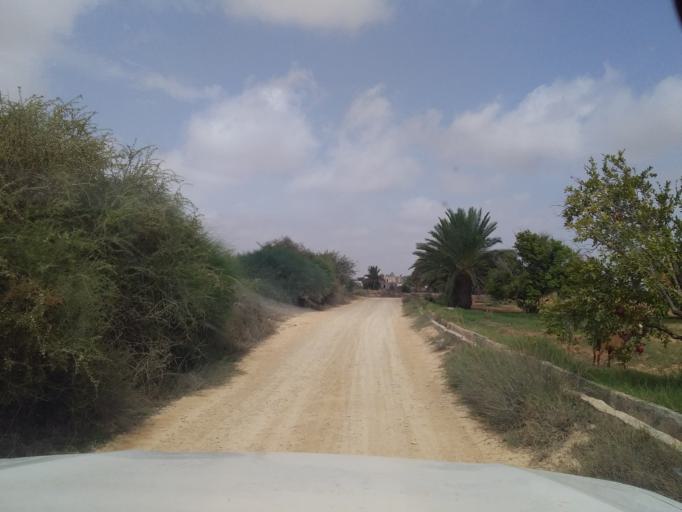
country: TN
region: Qabis
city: Gabes
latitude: 33.6271
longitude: 10.3076
